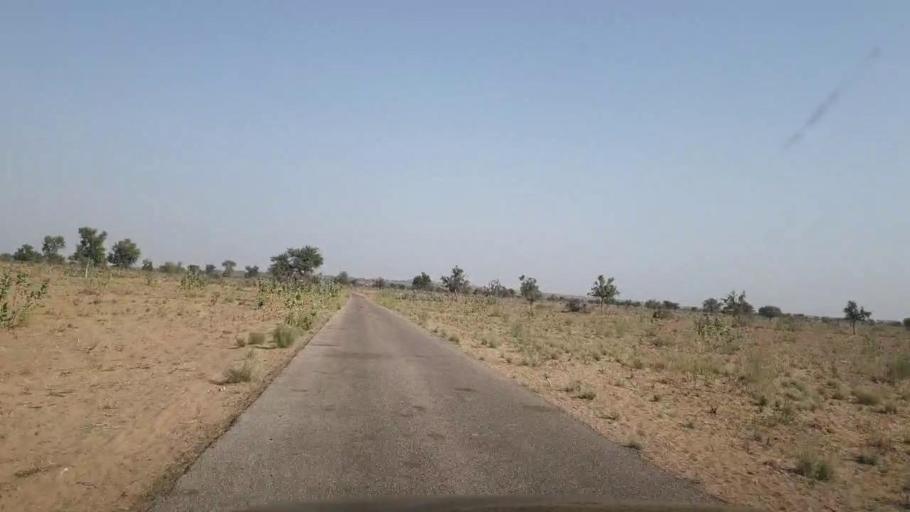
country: PK
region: Sindh
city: Islamkot
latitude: 25.1329
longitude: 70.4727
